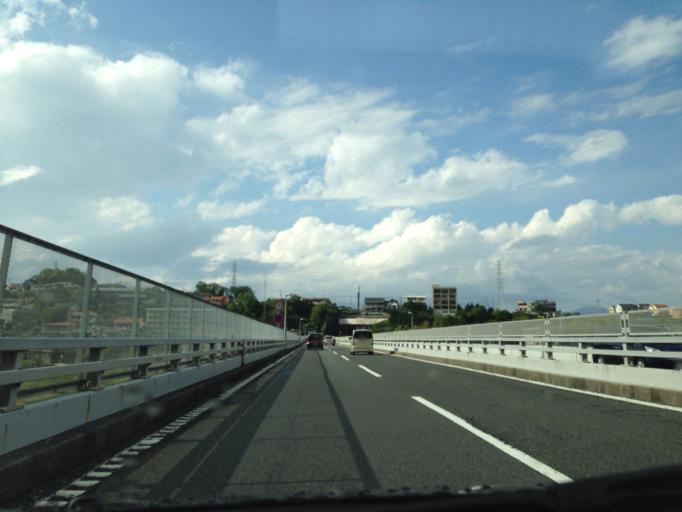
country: JP
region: Kanagawa
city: Odawara
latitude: 35.2711
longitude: 139.1504
